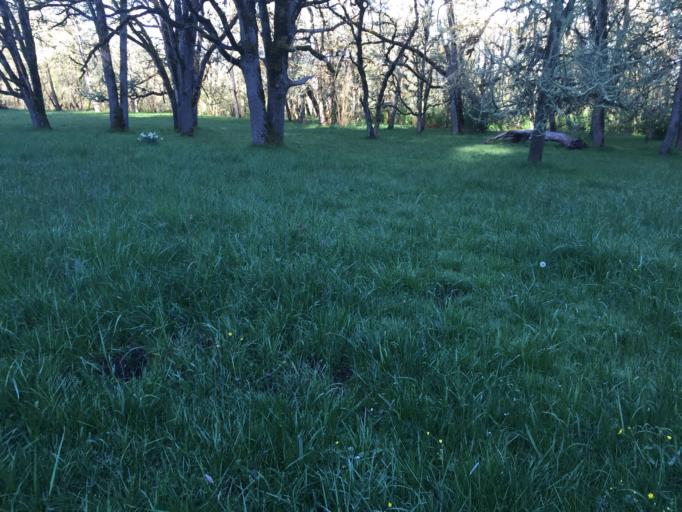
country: US
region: Oregon
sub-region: Lane County
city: Springfield
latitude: 44.0053
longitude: -122.9801
